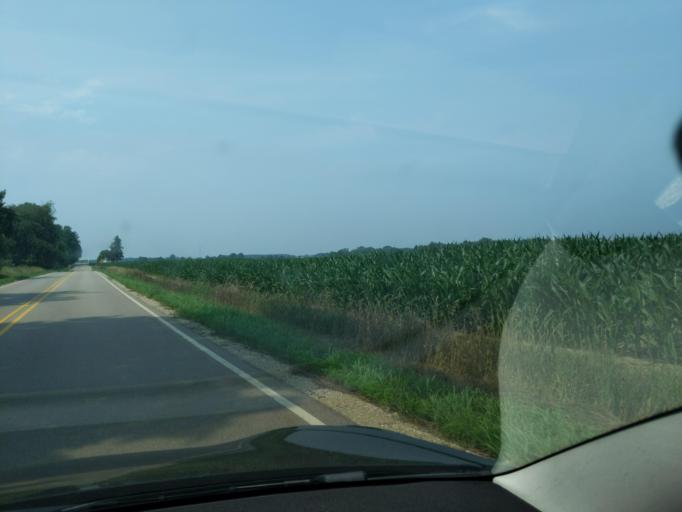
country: US
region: Michigan
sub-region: Clinton County
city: DeWitt
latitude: 42.9111
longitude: -84.5773
